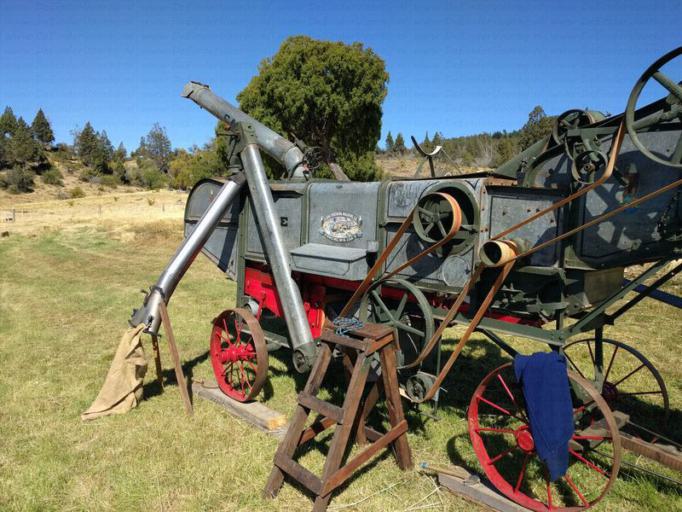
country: AR
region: Chubut
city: Trevelin
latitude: -43.2034
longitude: -71.5617
